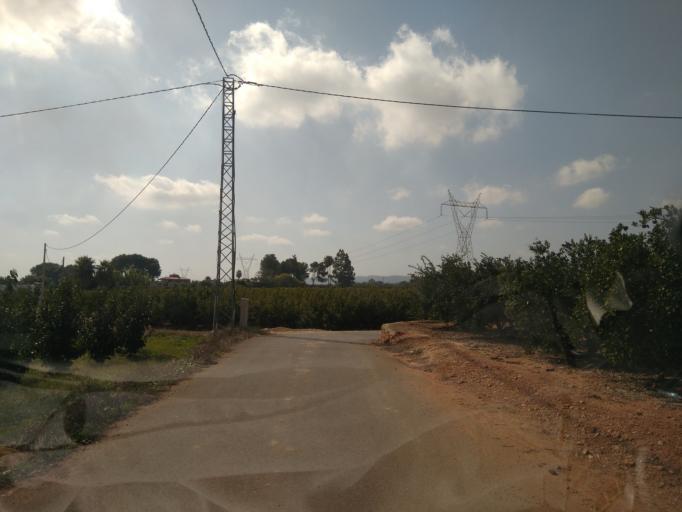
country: ES
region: Valencia
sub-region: Provincia de Valencia
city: Benimodo
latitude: 39.1809
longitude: -0.5492
